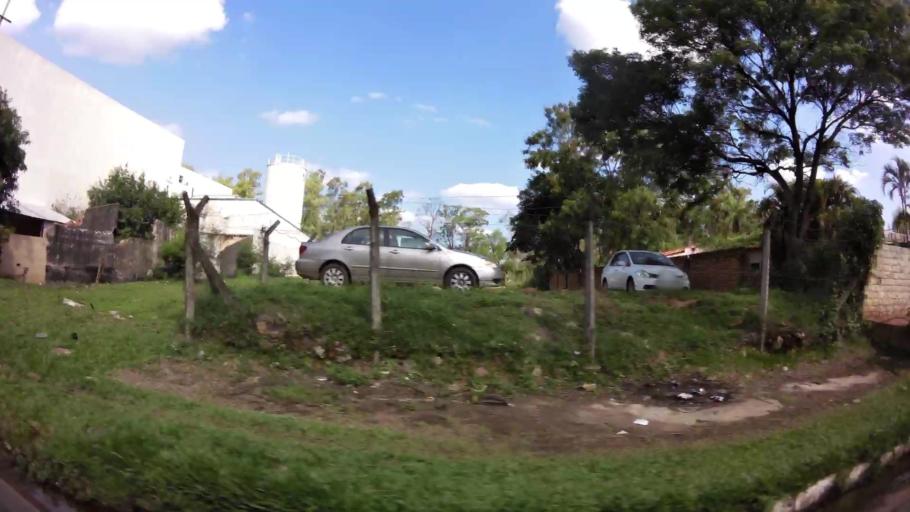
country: PY
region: Central
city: Fernando de la Mora
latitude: -25.3125
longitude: -57.5326
